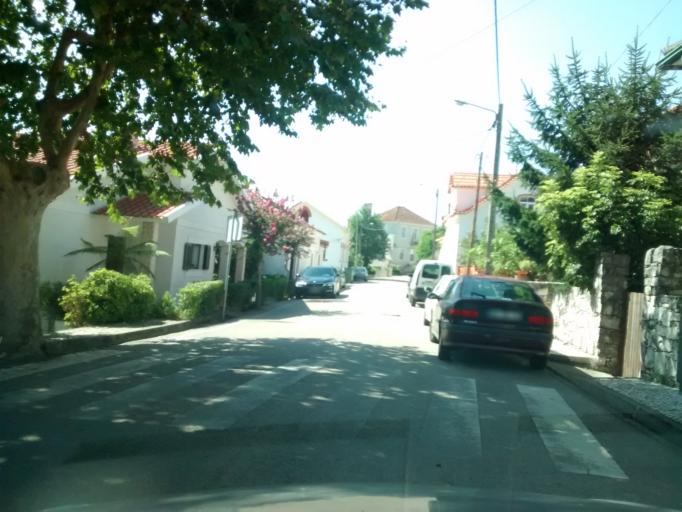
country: PT
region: Aveiro
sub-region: Mealhada
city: Pampilhosa do Botao
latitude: 40.3824
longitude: -8.3786
